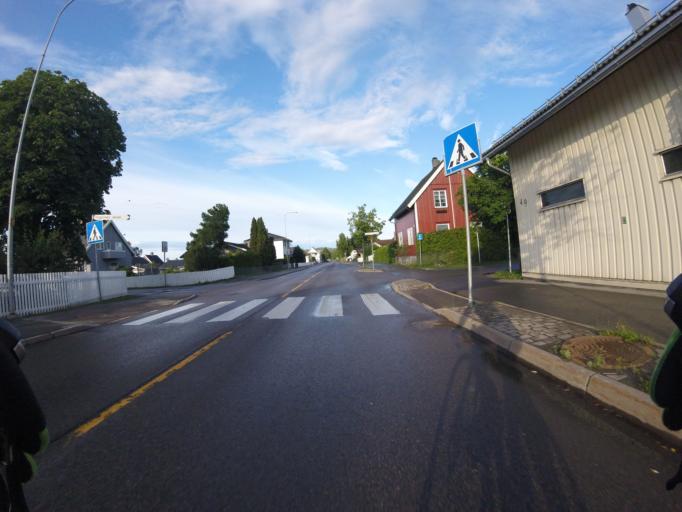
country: NO
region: Akershus
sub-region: Skedsmo
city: Lillestrom
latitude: 59.9554
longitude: 11.0664
